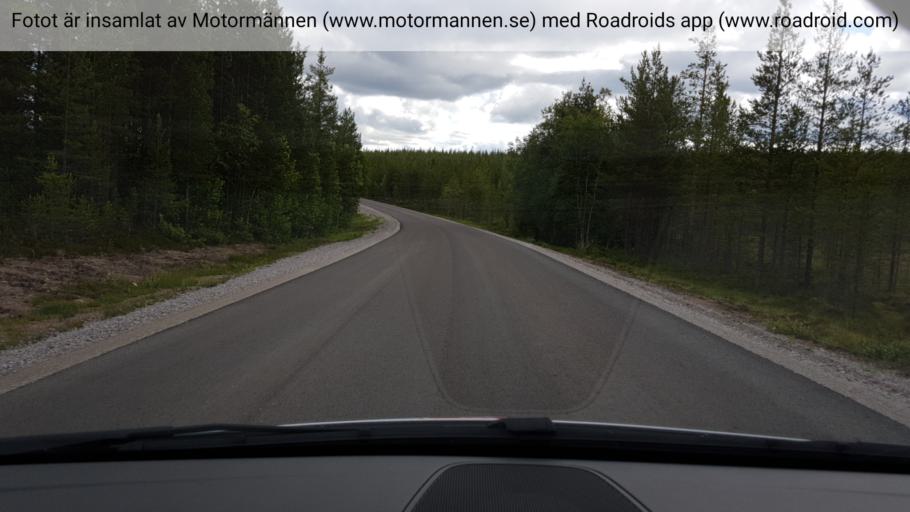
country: SE
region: Jaemtland
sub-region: Harjedalens Kommun
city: Sveg
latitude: 61.7115
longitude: 14.1690
